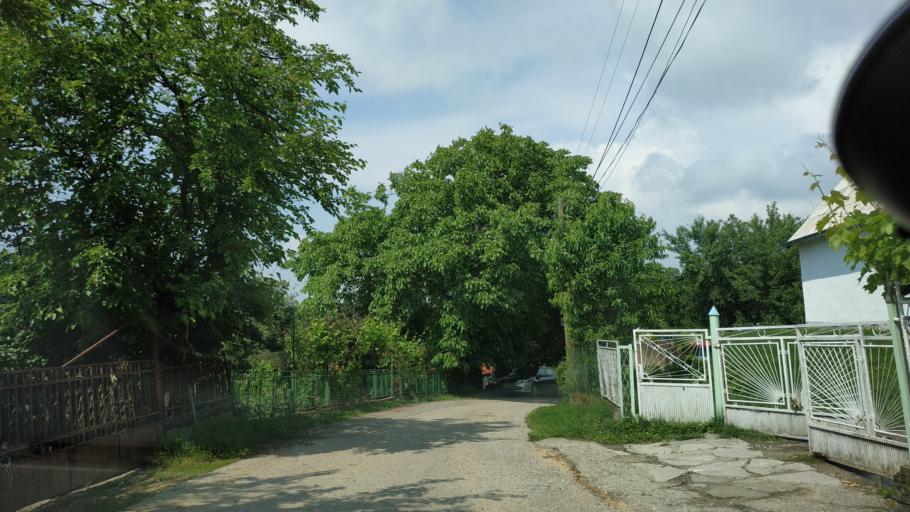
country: RS
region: Central Serbia
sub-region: Nisavski Okrug
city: Aleksinac
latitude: 43.4164
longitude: 21.7156
